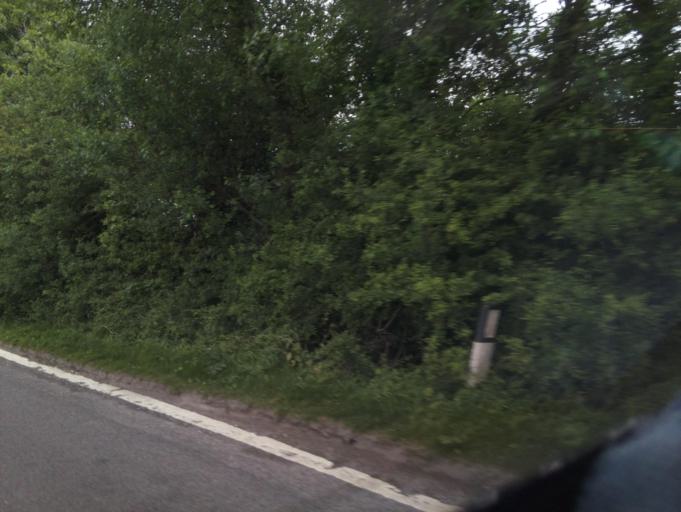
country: GB
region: England
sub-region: Staffordshire
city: Mayfield
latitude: 52.9813
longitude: -1.7488
